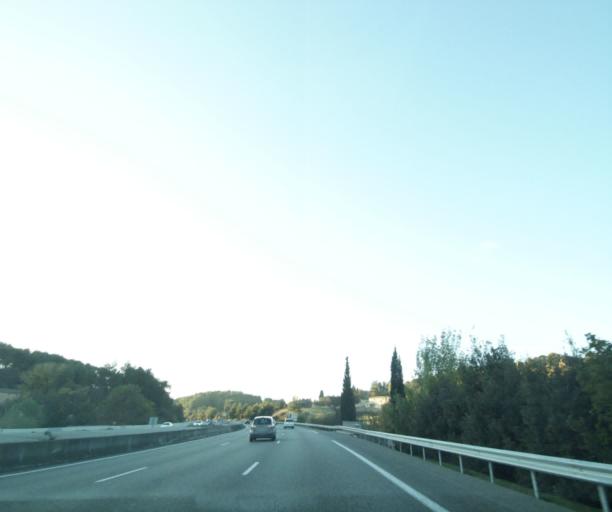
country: FR
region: Provence-Alpes-Cote d'Azur
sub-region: Departement des Bouches-du-Rhone
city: Le Tholonet
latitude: 43.5122
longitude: 5.4949
